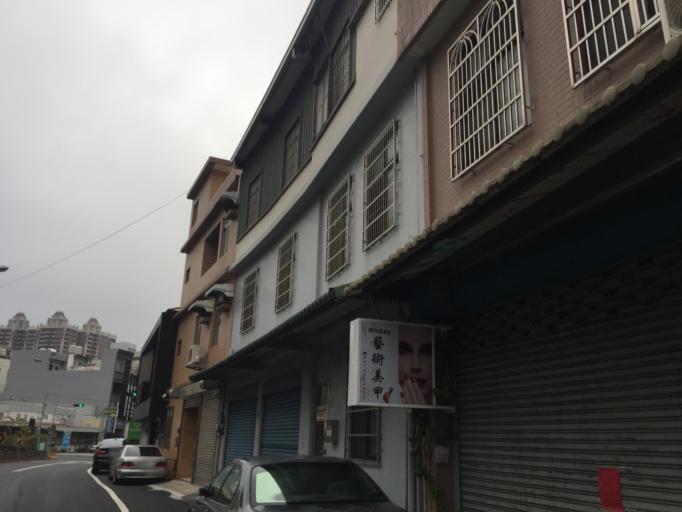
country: TW
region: Taiwan
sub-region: Hsinchu
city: Zhubei
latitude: 24.8179
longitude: 121.0251
